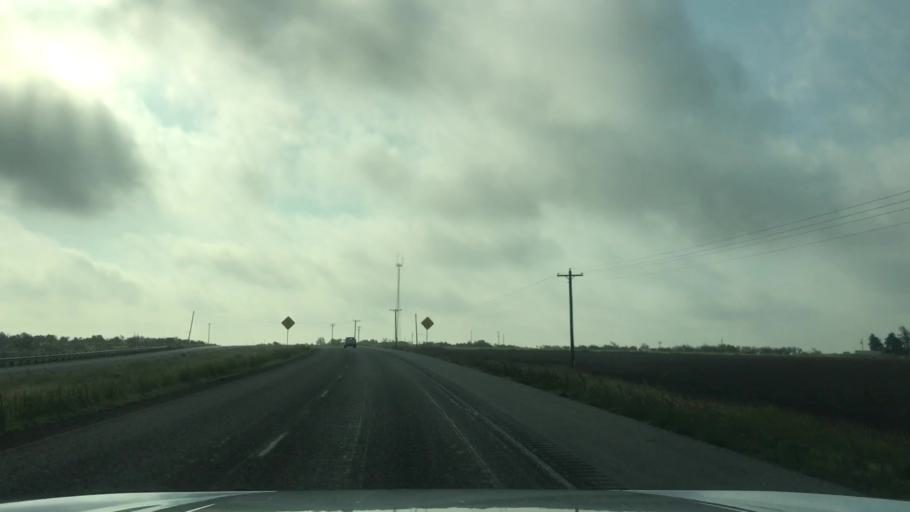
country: US
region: Texas
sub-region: Garza County
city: Post
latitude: 33.2154
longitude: -101.4287
